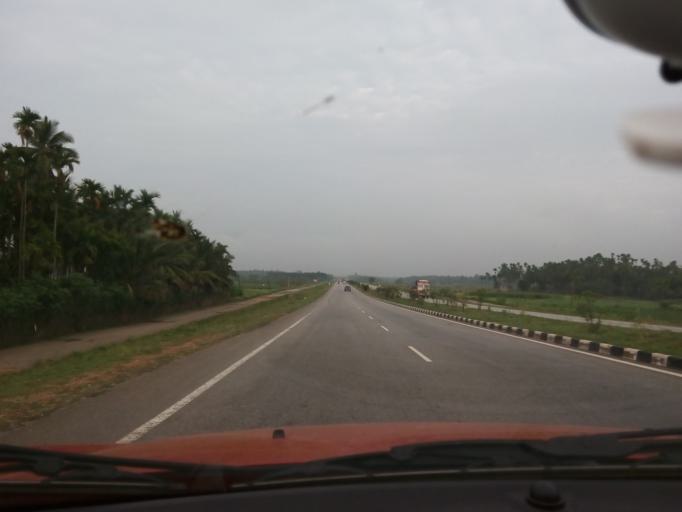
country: IN
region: Karnataka
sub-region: Tumkur
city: Kunigal
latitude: 13.0050
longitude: 77.0042
